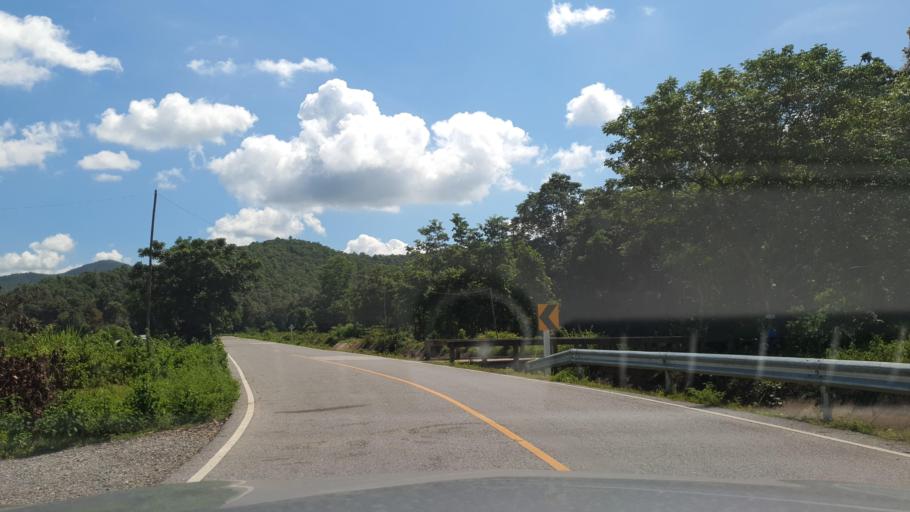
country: TH
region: Chiang Mai
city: Mae On
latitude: 18.7736
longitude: 99.1870
